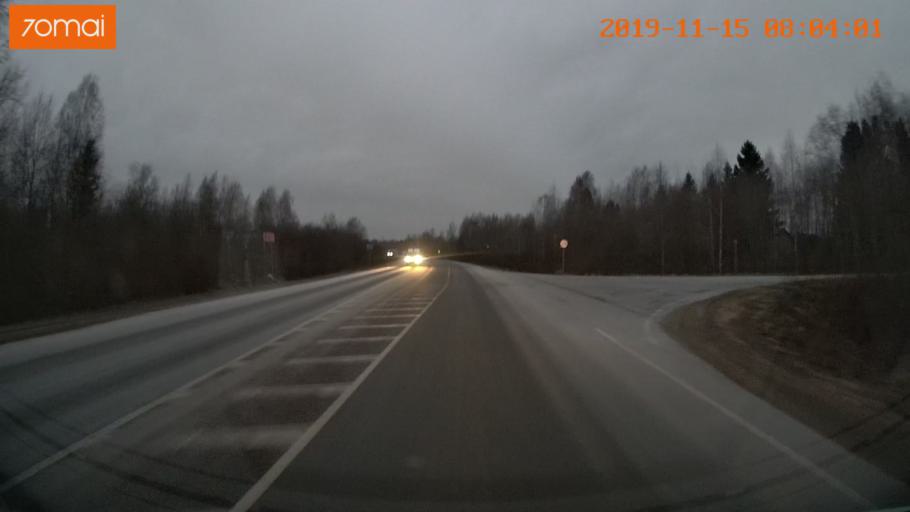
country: RU
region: Vologda
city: Cherepovets
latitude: 59.0038
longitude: 38.0824
